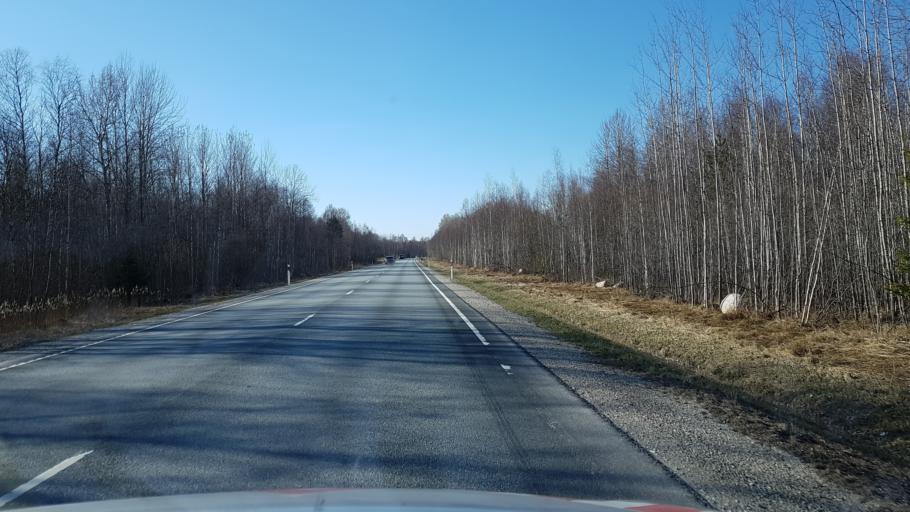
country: EE
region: Jogevamaa
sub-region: Mustvee linn
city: Mustvee
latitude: 58.8365
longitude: 26.9280
